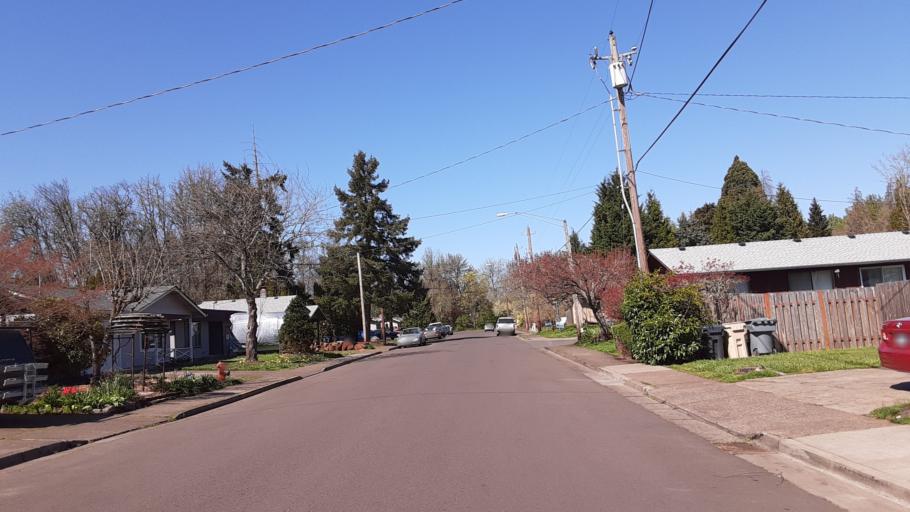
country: US
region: Oregon
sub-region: Benton County
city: Corvallis
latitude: 44.5437
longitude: -123.2586
